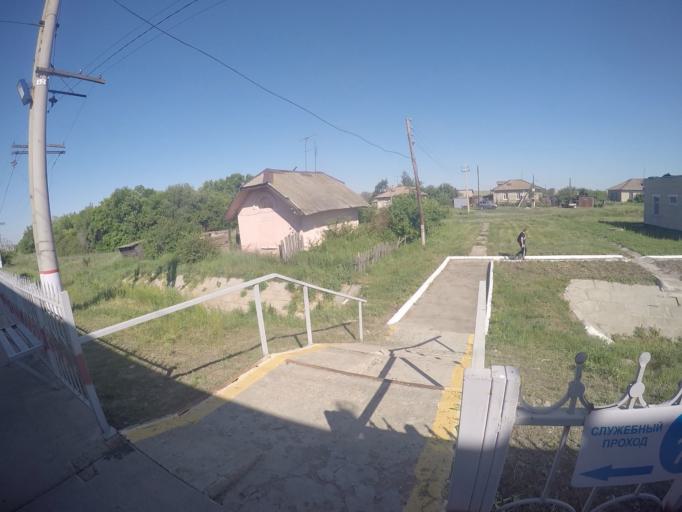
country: RU
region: Saratov
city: Krasnoarmeysk
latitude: 51.2575
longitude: 45.5922
